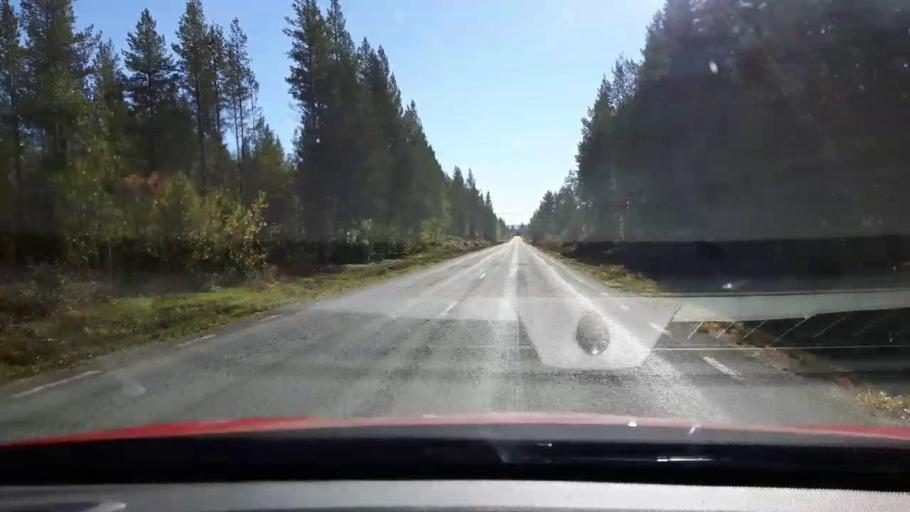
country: SE
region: Jaemtland
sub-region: Harjedalens Kommun
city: Sveg
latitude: 62.3720
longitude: 13.9823
